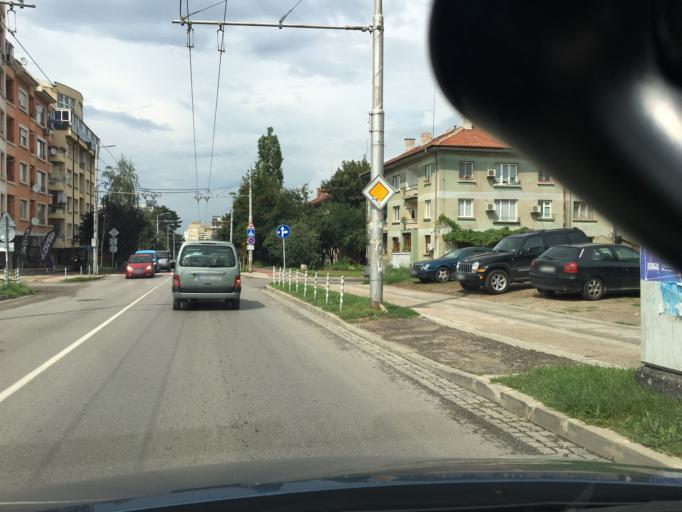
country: BG
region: Sofia-Capital
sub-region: Stolichna Obshtina
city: Sofia
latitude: 42.6627
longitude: 23.2741
